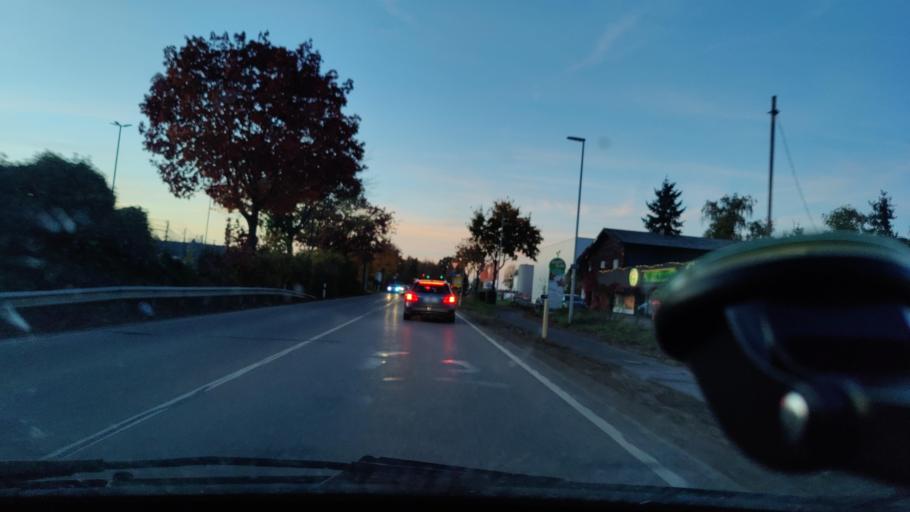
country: DE
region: North Rhine-Westphalia
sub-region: Regierungsbezirk Koln
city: Heinsberg
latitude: 51.0688
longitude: 6.1125
